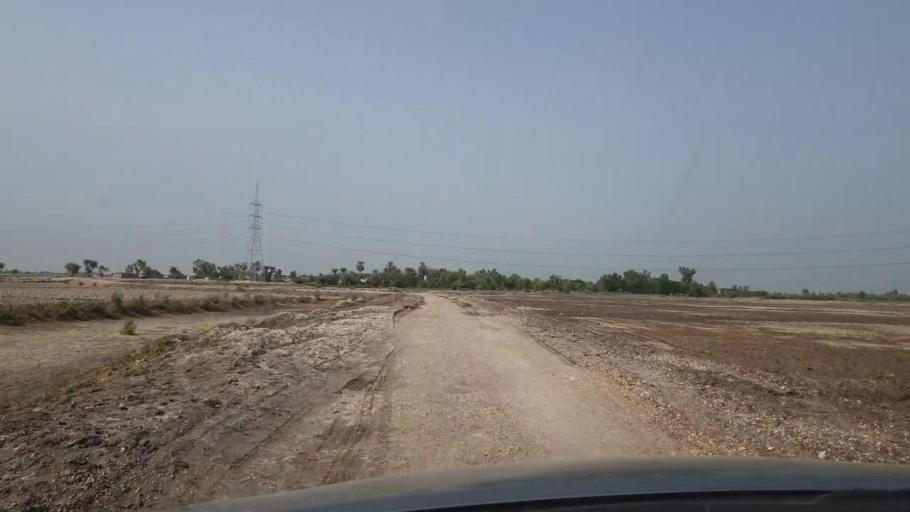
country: PK
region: Sindh
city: Lakhi
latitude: 27.8305
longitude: 68.6973
